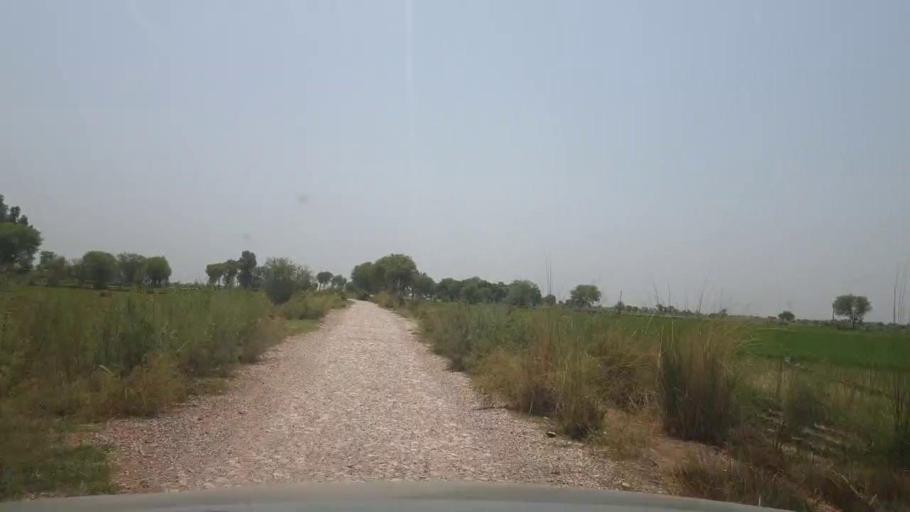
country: PK
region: Sindh
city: Lakhi
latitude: 27.8486
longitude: 68.6647
